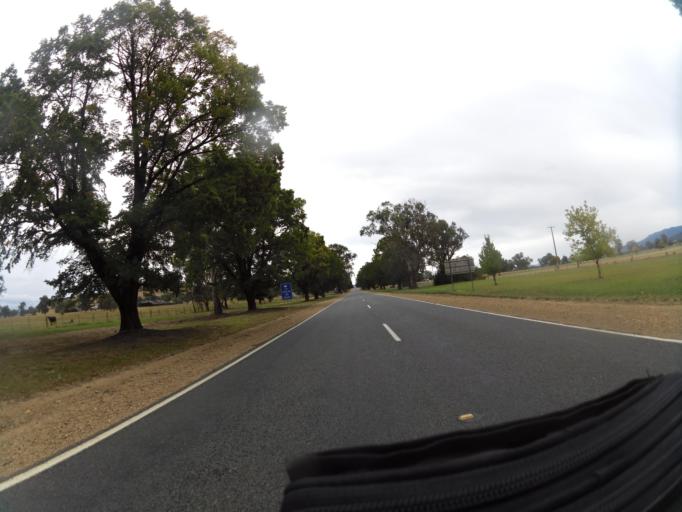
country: AU
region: New South Wales
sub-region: Snowy River
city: Jindabyne
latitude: -36.1834
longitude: 147.9219
